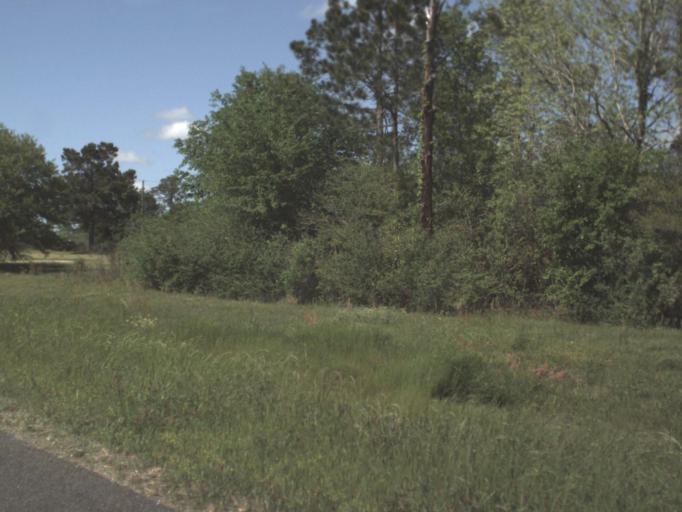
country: US
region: Florida
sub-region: Escambia County
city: Cantonment
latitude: 30.6255
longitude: -87.3290
